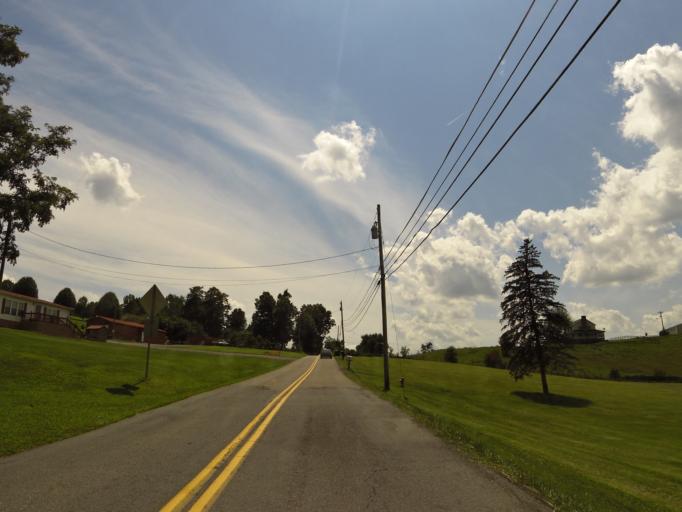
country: US
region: Virginia
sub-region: Washington County
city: Abingdon
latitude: 36.6906
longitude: -81.9238
